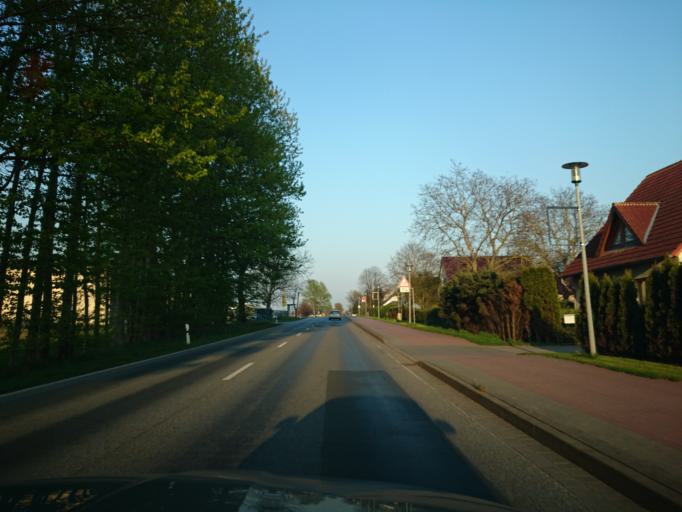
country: DE
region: Mecklenburg-Vorpommern
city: Broderstorf
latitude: 54.0799
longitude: 12.2375
